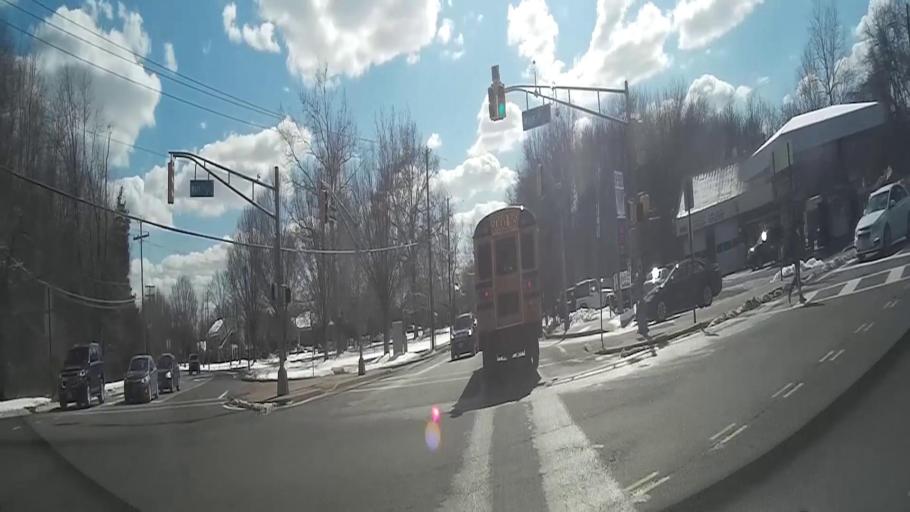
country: US
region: New Jersey
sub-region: Burlington County
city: Marlton
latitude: 39.8845
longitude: -74.9050
